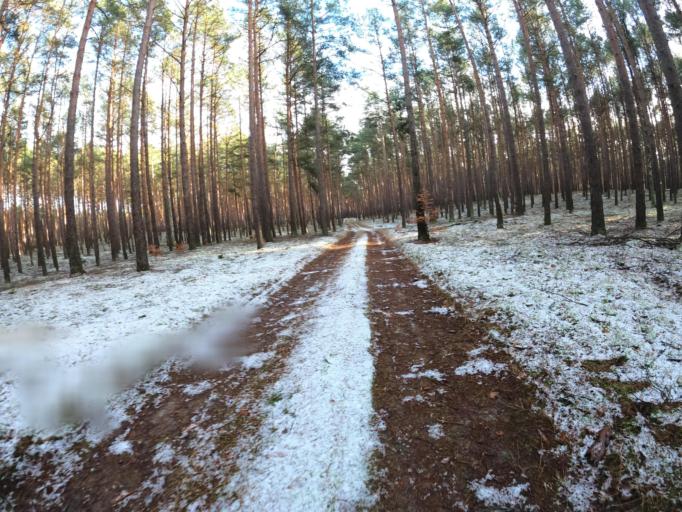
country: PL
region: Lubusz
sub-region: Powiat slubicki
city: Cybinka
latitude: 52.2344
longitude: 14.8277
